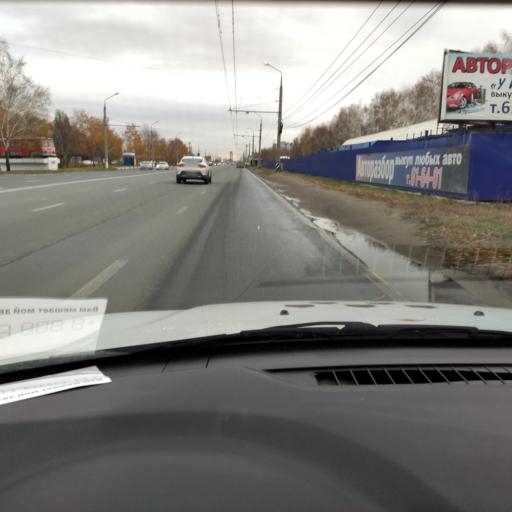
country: RU
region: Samara
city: Tol'yatti
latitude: 53.5515
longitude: 49.3081
